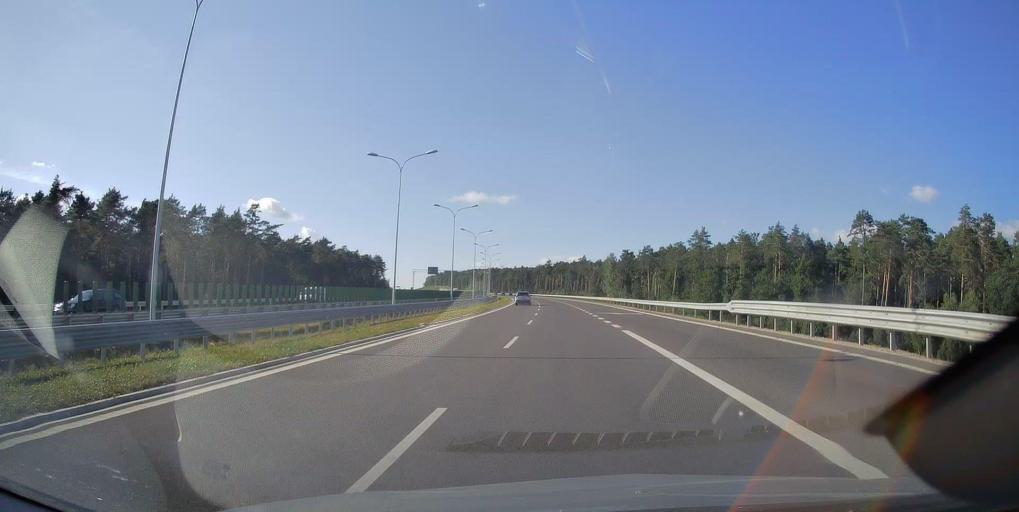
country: PL
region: Swietokrzyskie
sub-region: Powiat skarzyski
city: Skarzysko-Kamienna
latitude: 51.1214
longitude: 20.8467
